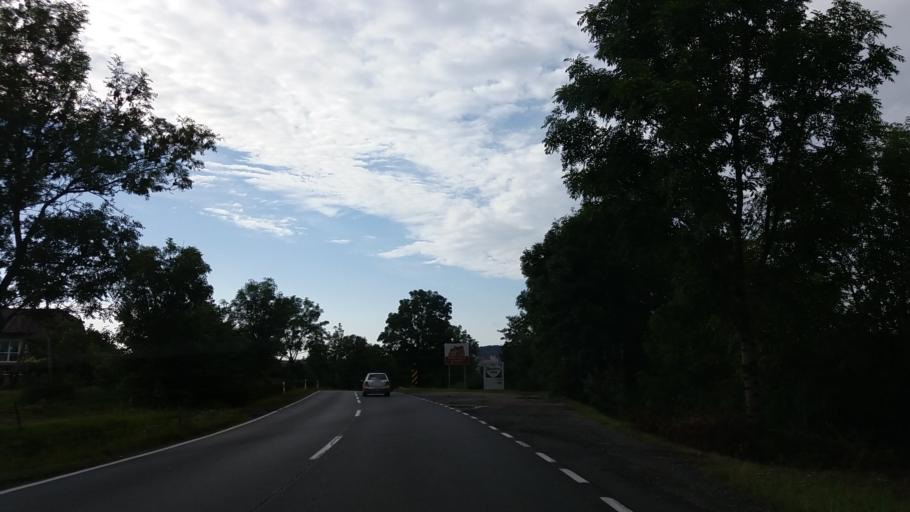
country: PL
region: Lower Silesian Voivodeship
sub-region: Powiat swidnicki
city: Strzegom
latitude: 50.9506
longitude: 16.3596
